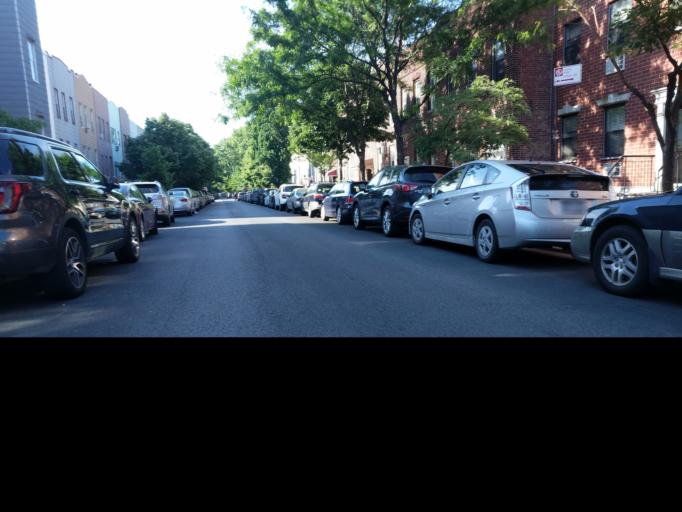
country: US
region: New York
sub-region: Queens County
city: Long Island City
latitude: 40.7218
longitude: -73.9439
